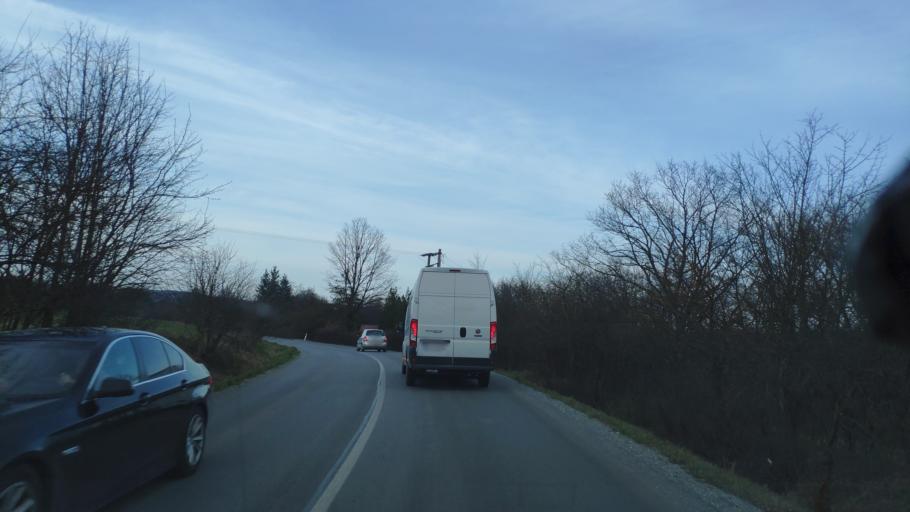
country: SK
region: Kosicky
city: Kosice
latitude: 48.7836
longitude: 21.2425
